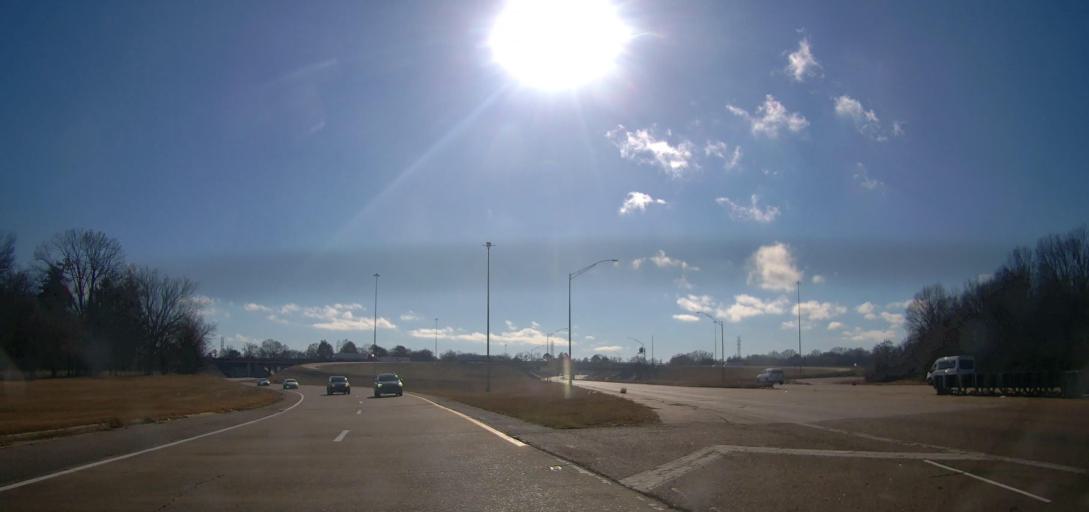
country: US
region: Tennessee
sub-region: Shelby County
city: Bartlett
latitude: 35.1957
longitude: -89.9254
